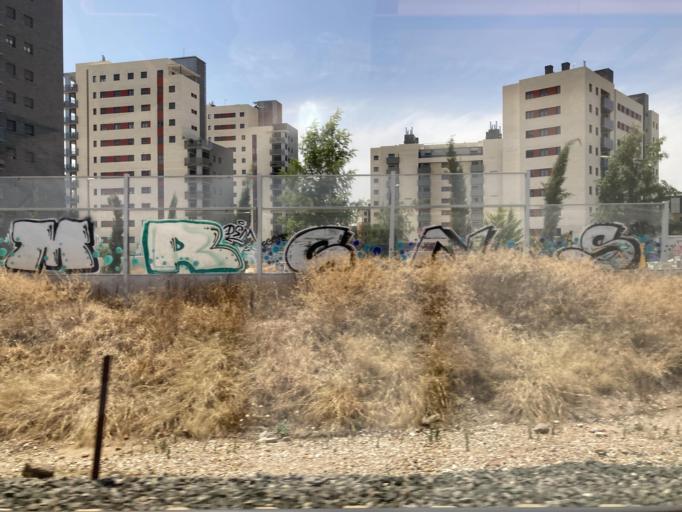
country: ES
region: Andalusia
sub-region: Provincia de Sevilla
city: Sevilla
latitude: 37.3555
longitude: -5.9729
